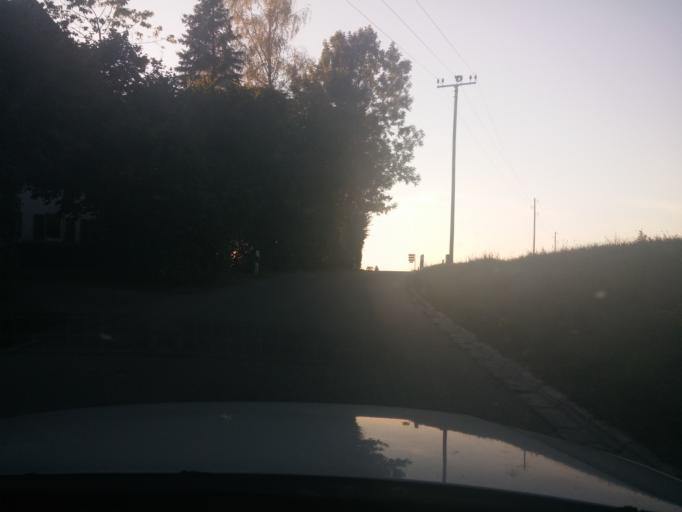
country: DE
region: Bavaria
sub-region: Swabia
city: Altusried
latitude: 47.8286
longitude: 10.1756
